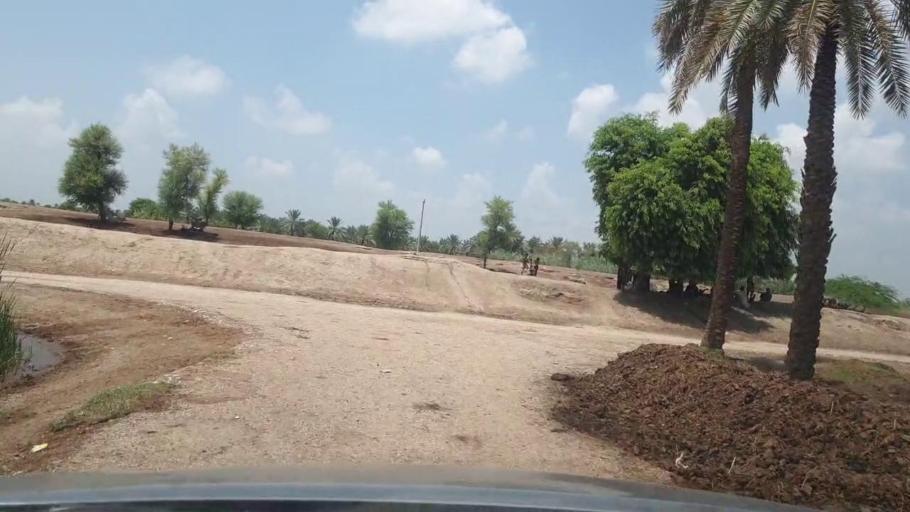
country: PK
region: Sindh
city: Pir jo Goth
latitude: 27.6133
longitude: 68.6040
